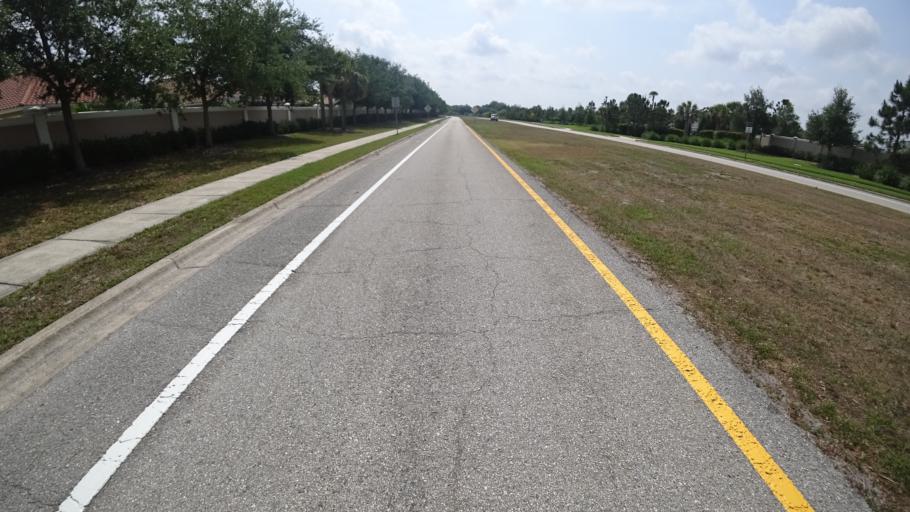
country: US
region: Florida
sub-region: Sarasota County
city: North Sarasota
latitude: 27.4194
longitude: -82.5125
